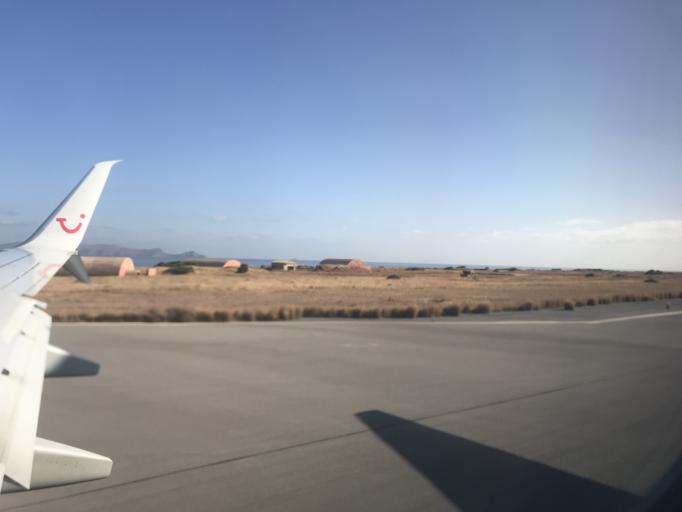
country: GR
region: Crete
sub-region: Nomos Irakleiou
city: Nea Alikarnassos
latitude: 35.3395
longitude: 25.1801
